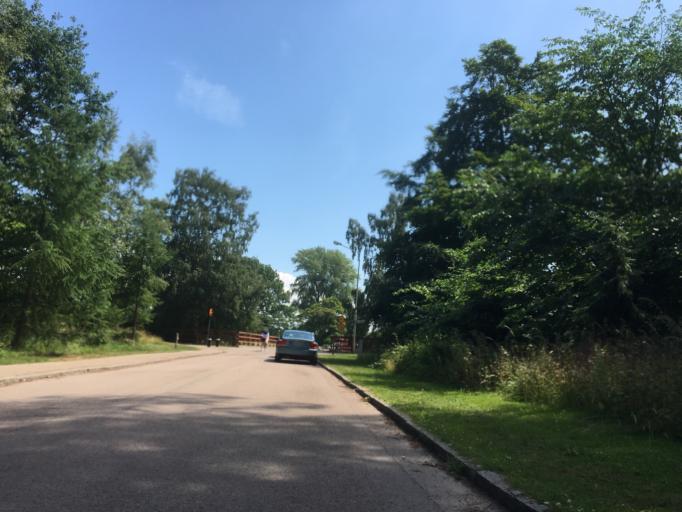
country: SE
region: Skane
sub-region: Landskrona
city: Landskrona
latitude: 55.8770
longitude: 12.8215
